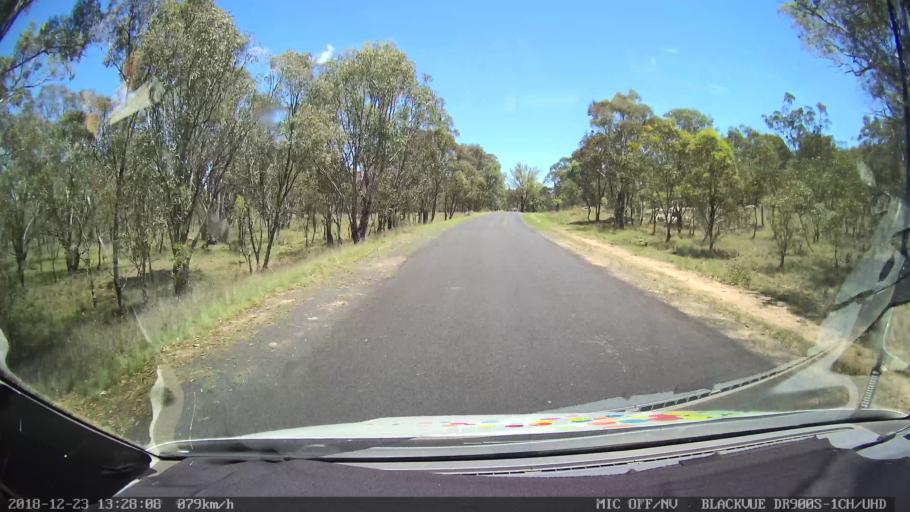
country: AU
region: New South Wales
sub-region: Armidale Dumaresq
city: Armidale
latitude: -30.4645
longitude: 151.3520
